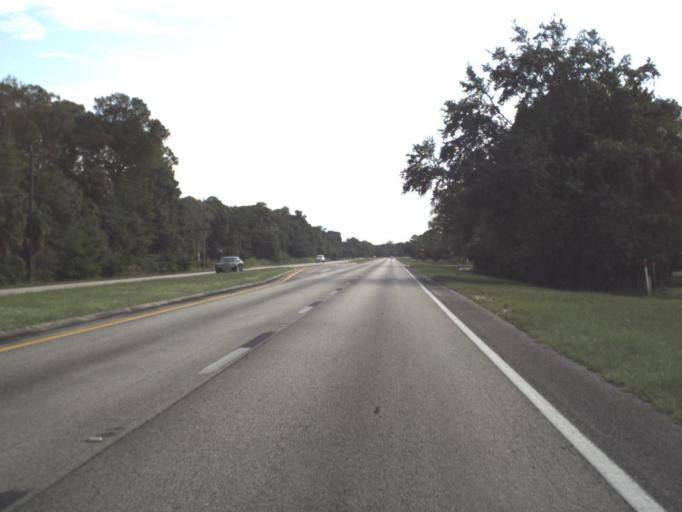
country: US
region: Florida
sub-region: Lee County
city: Olga
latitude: 26.7136
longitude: -81.7019
